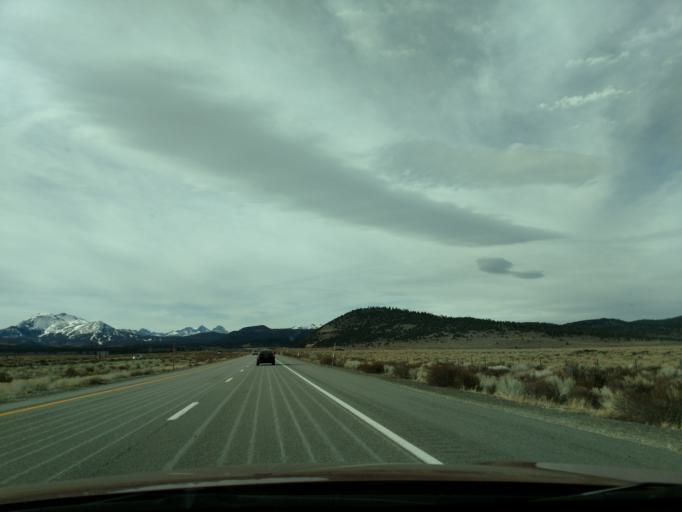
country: US
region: California
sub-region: Mono County
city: Mammoth Lakes
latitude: 37.6301
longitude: -118.8673
